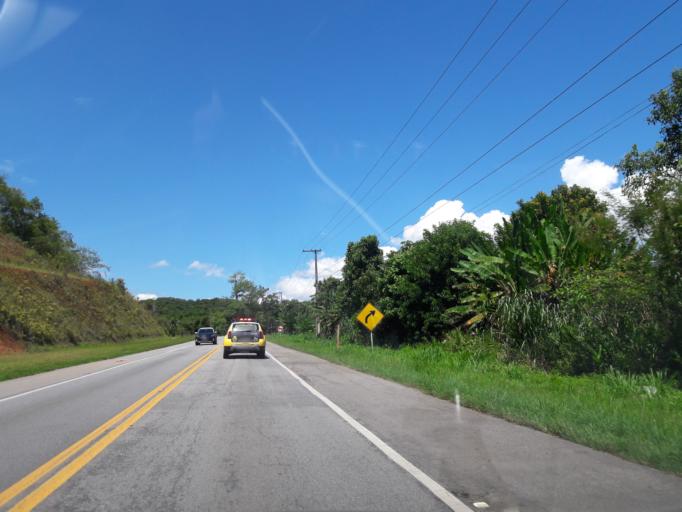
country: BR
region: Parana
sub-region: Antonina
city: Antonina
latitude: -25.5190
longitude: -48.8006
